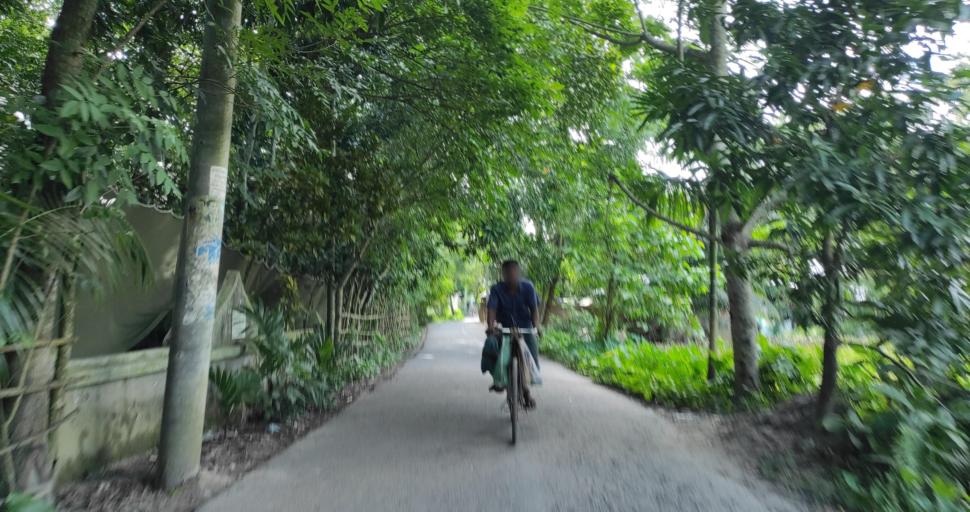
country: BD
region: Barisal
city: Gaurnadi
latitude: 22.8929
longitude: 90.1938
